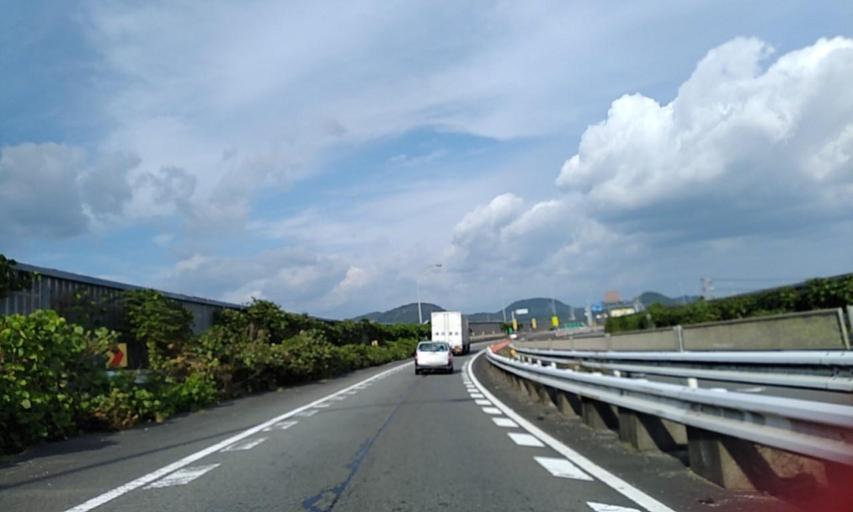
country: JP
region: Shizuoka
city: Kanaya
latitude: 34.8374
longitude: 138.1176
